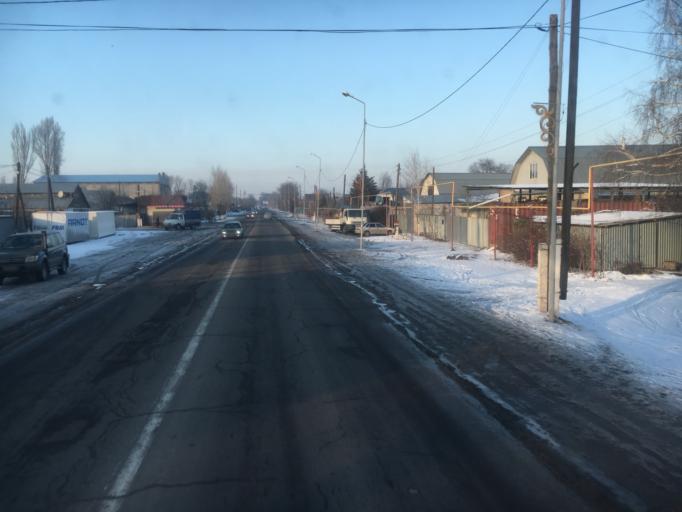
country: KZ
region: Almaty Oblysy
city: Burunday
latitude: 43.3688
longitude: 76.6414
